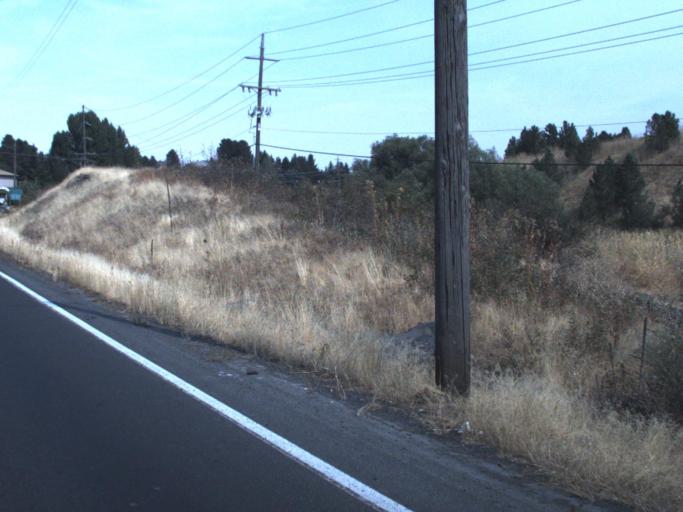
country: US
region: Washington
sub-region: Whitman County
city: Pullman
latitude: 46.7462
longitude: -117.1720
